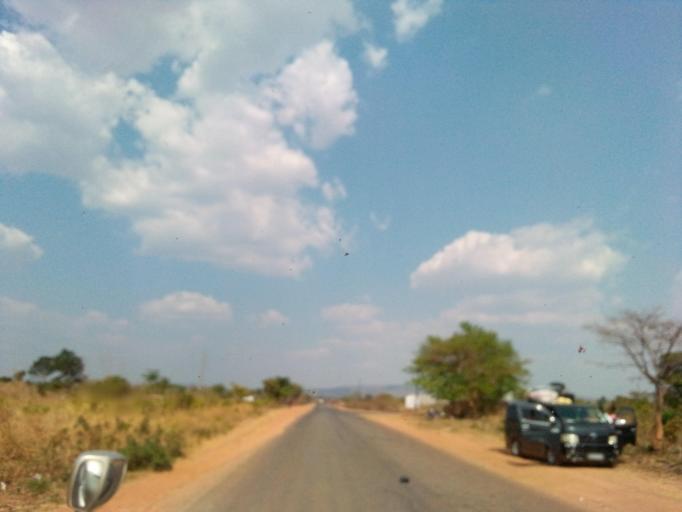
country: ZM
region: Northern
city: Mpika
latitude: -11.8331
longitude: 31.4088
